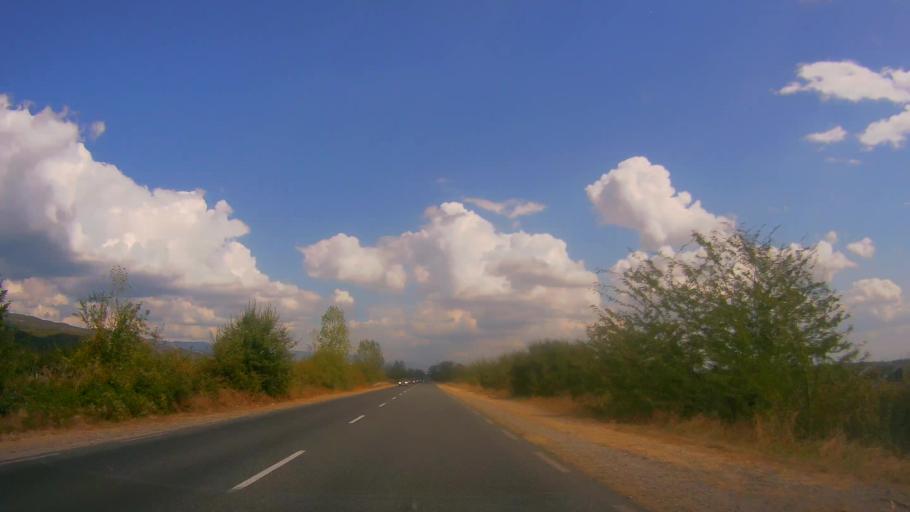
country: BG
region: Sliven
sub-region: Obshtina Sliven
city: Sliven
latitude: 42.6334
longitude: 26.2035
